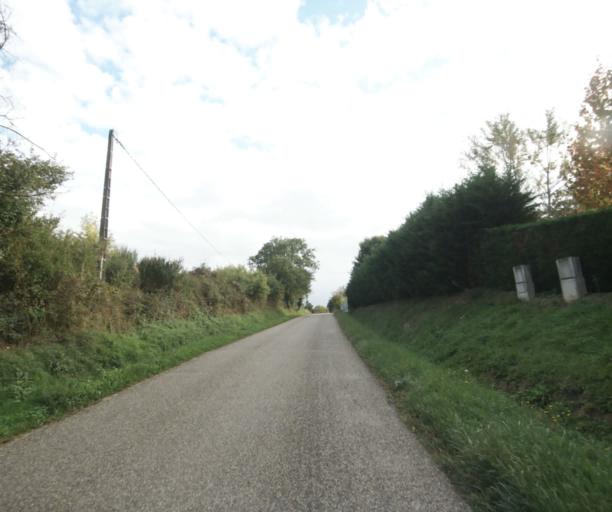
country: FR
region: Midi-Pyrenees
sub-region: Departement du Gers
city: Eauze
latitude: 43.8706
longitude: 0.1009
